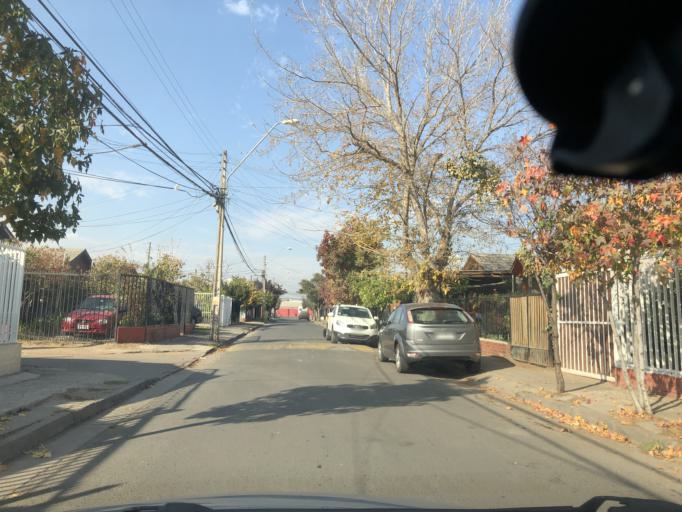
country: CL
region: Santiago Metropolitan
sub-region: Provincia de Cordillera
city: Puente Alto
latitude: -33.5902
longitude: -70.5751
